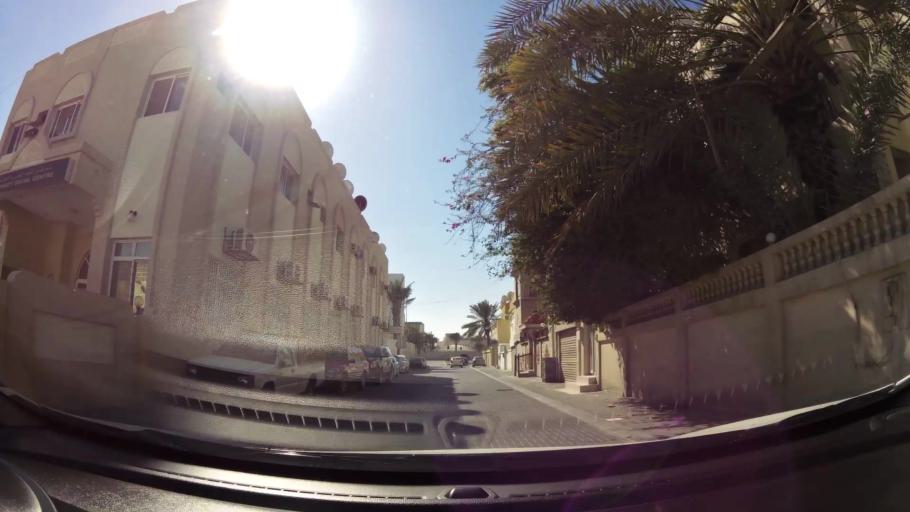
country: BH
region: Muharraq
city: Al Hadd
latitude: 26.2423
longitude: 50.6526
